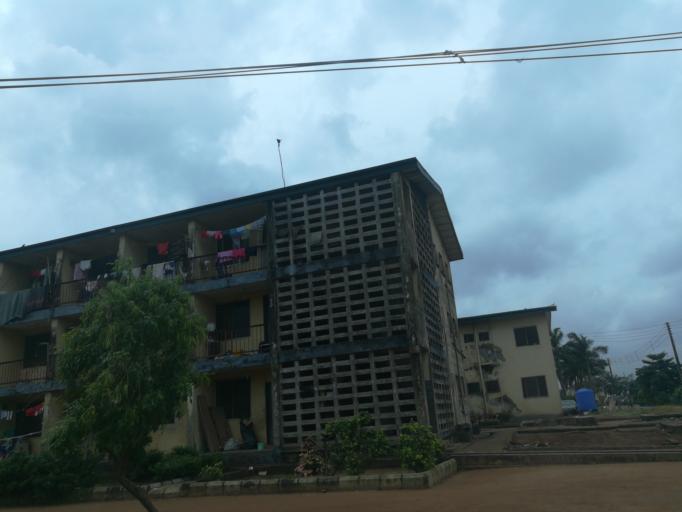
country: NG
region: Lagos
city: Oshodi
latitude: 6.5704
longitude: 3.3541
